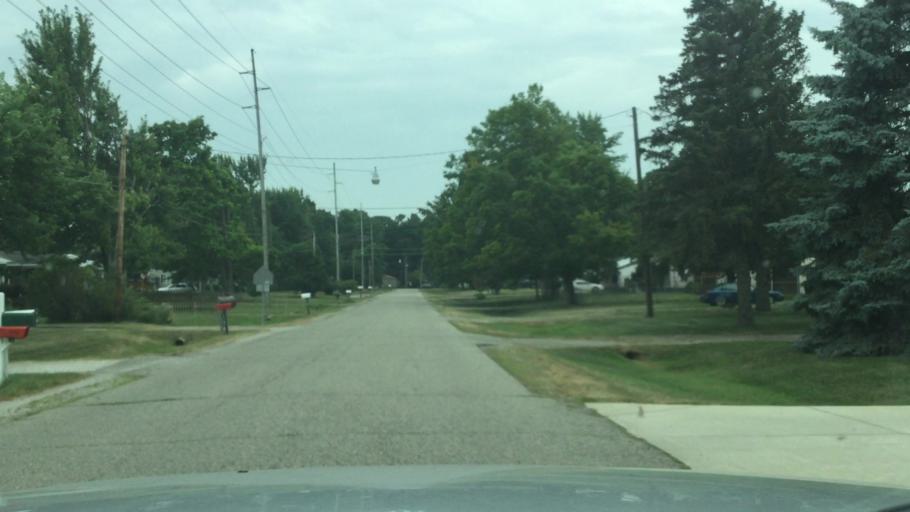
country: US
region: Michigan
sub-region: Genesee County
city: Flint
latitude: 42.9696
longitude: -83.7029
